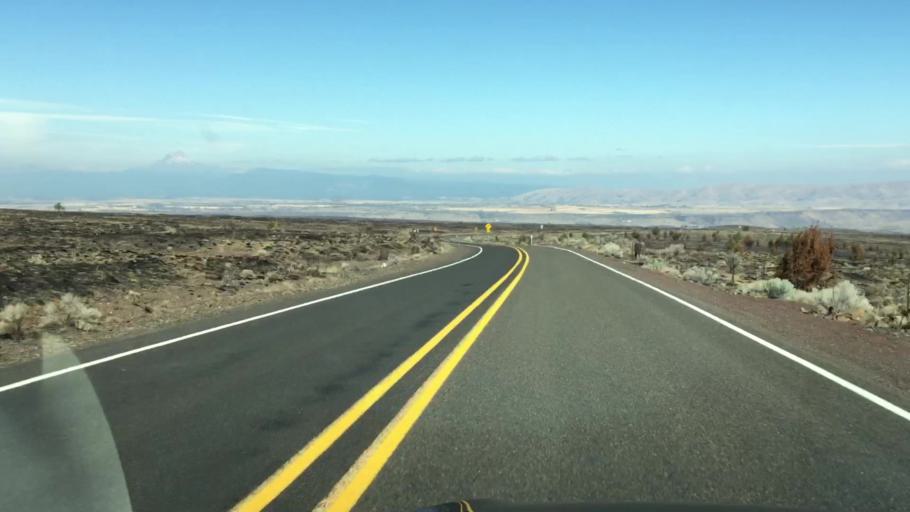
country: US
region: Oregon
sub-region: Jefferson County
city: Warm Springs
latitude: 45.0954
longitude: -121.0318
